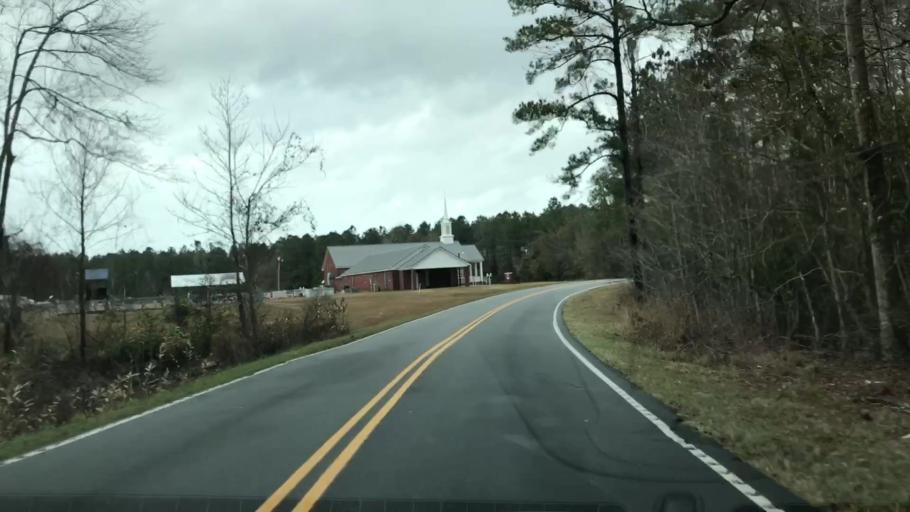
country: US
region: South Carolina
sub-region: Florence County
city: Johnsonville
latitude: 33.6549
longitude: -79.3041
